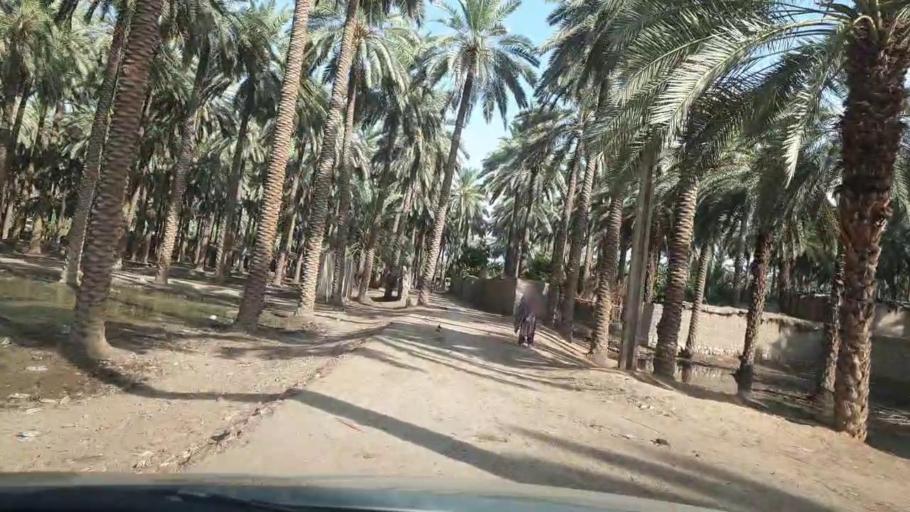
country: PK
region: Sindh
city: Sukkur
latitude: 27.6591
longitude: 68.8308
